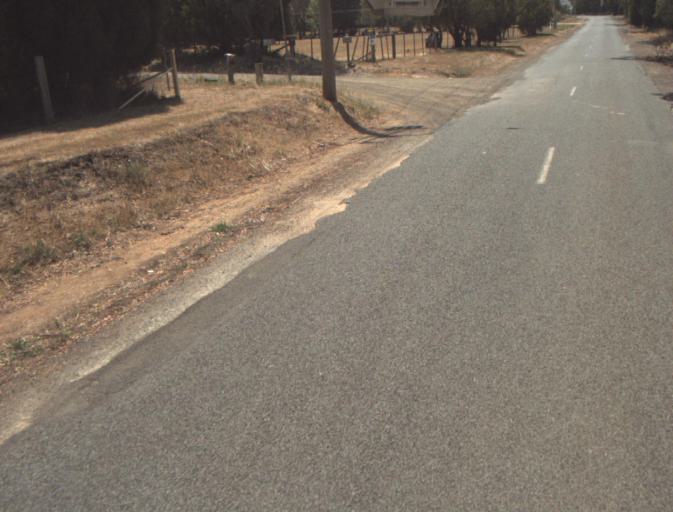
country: AU
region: Tasmania
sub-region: Launceston
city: Newstead
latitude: -41.5001
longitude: 147.2064
